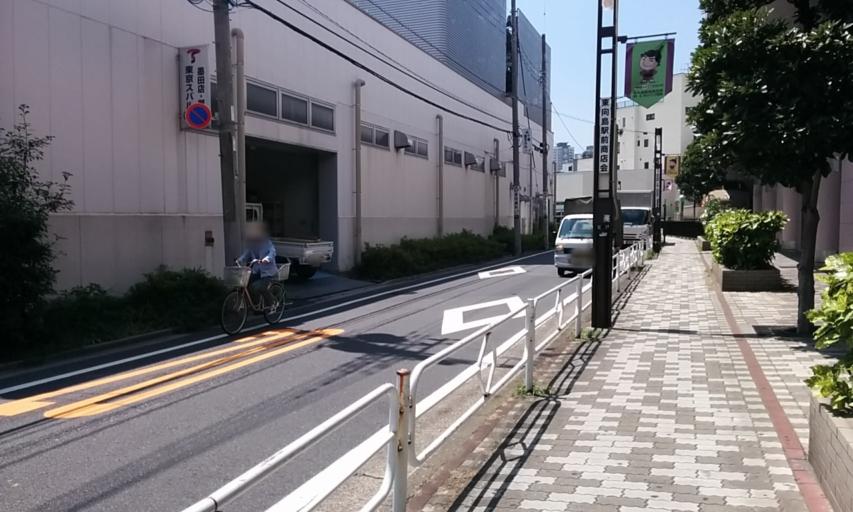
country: JP
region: Tokyo
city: Urayasu
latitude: 35.7246
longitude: 139.8195
